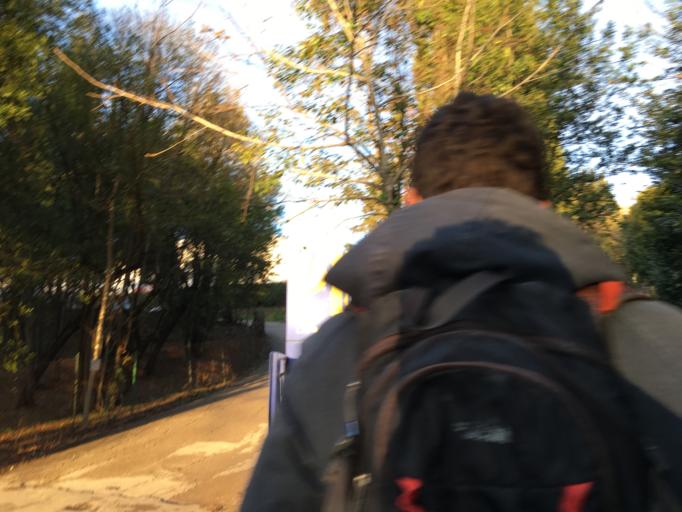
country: IT
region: Umbria
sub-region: Provincia di Perugia
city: Perugia
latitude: 43.1065
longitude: 12.3807
